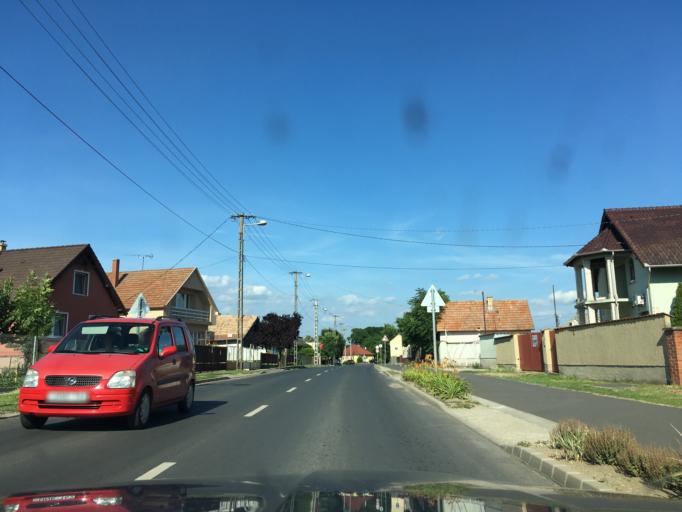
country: HU
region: Hajdu-Bihar
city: Hajdusamson
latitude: 47.5993
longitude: 21.7509
